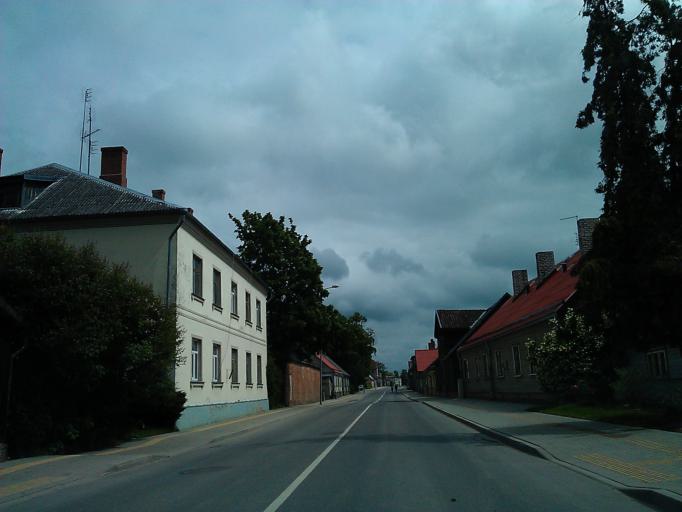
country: LV
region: Aizpute
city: Aizpute
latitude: 56.7180
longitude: 21.6070
